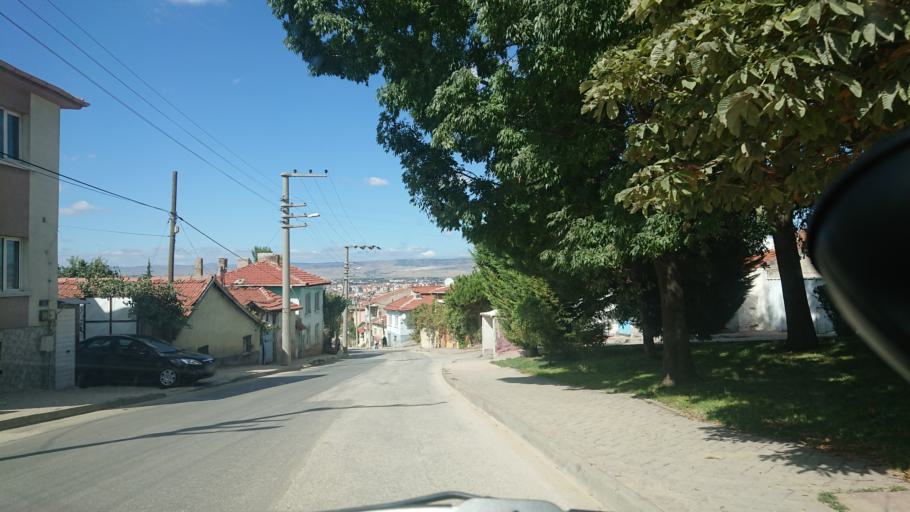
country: TR
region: Eskisehir
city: Eskisehir
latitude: 39.7597
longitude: 30.5298
